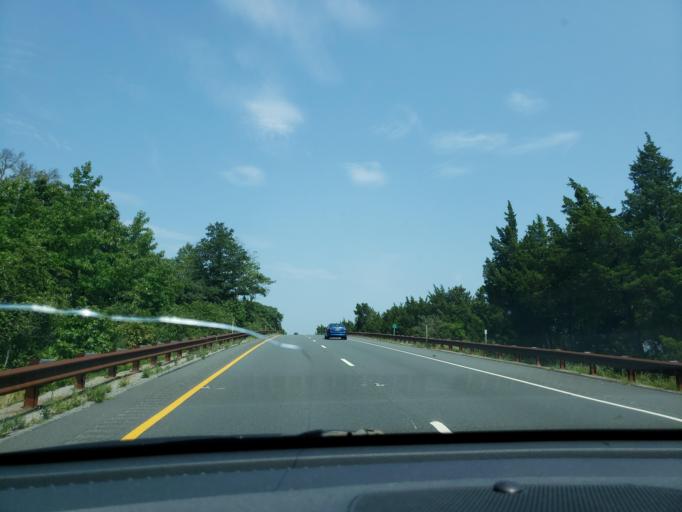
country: US
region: New Jersey
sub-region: Cape May County
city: Sea Isle City
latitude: 39.2345
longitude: -74.6688
